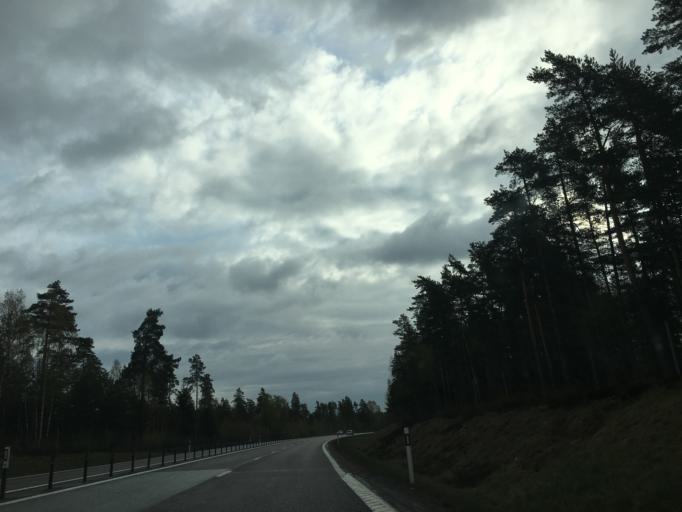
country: SE
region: Vaermland
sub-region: Karlstads Kommun
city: Skattkarr
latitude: 59.4192
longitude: 13.6702
